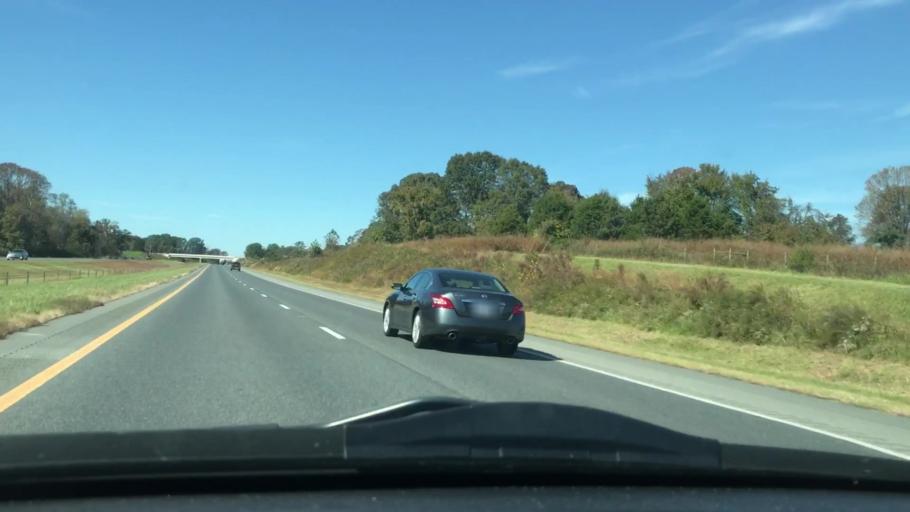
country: US
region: North Carolina
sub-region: Randolph County
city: Randleman
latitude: 35.8507
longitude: -79.8752
